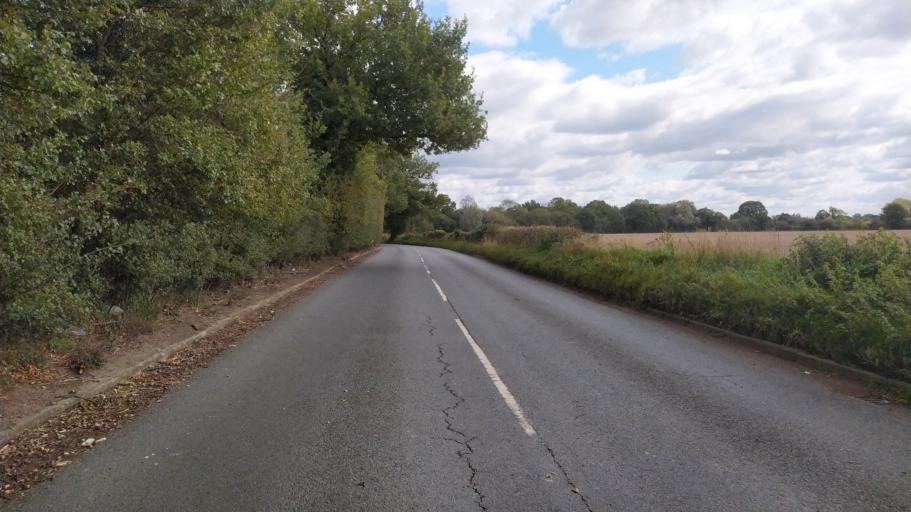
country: GB
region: England
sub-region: Wokingham
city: Shinfield
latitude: 51.4138
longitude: -0.9864
